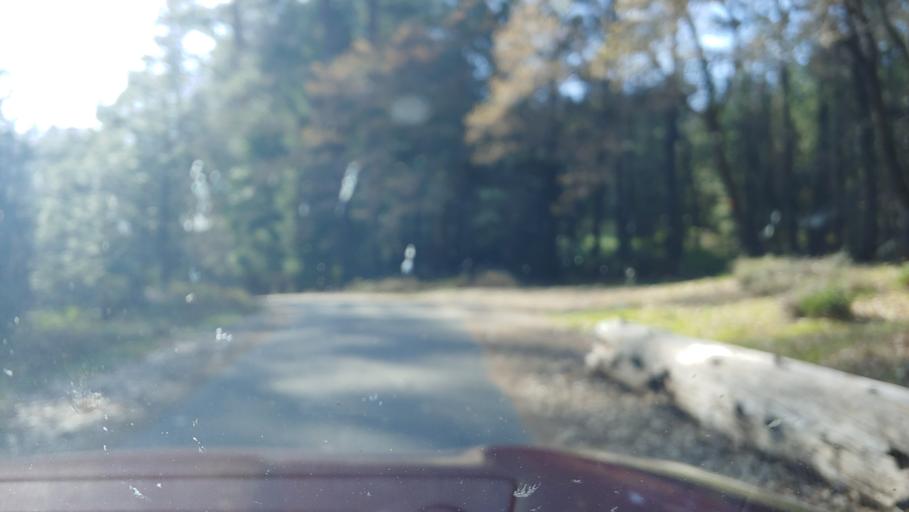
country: US
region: California
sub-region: Siskiyou County
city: Dunsmuir
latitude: 40.9976
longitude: -122.4117
